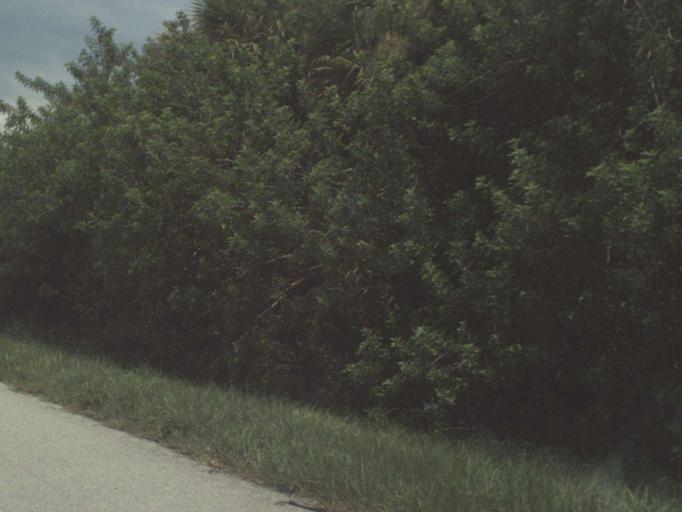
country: US
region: Florida
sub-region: Okeechobee County
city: Taylor Creek
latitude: 27.1167
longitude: -80.6701
